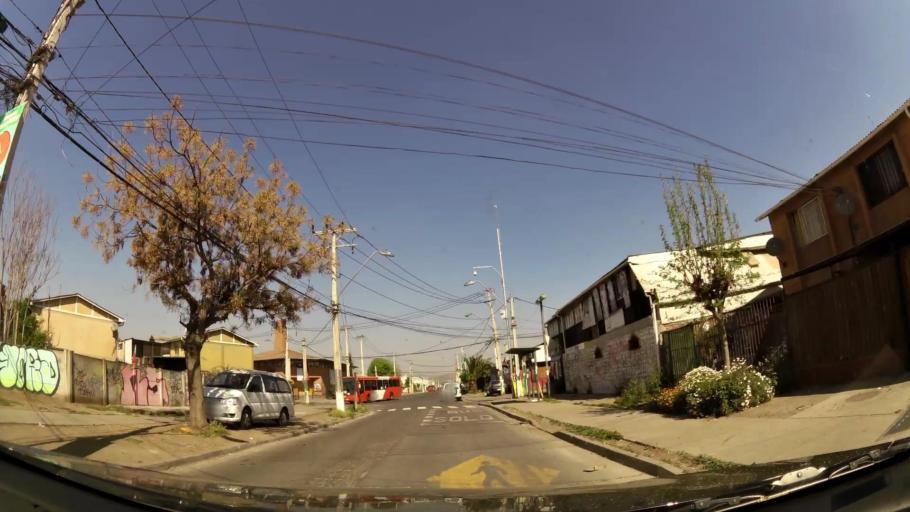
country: CL
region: Santiago Metropolitan
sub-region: Provincia de Santiago
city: Lo Prado
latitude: -33.3542
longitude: -70.7500
